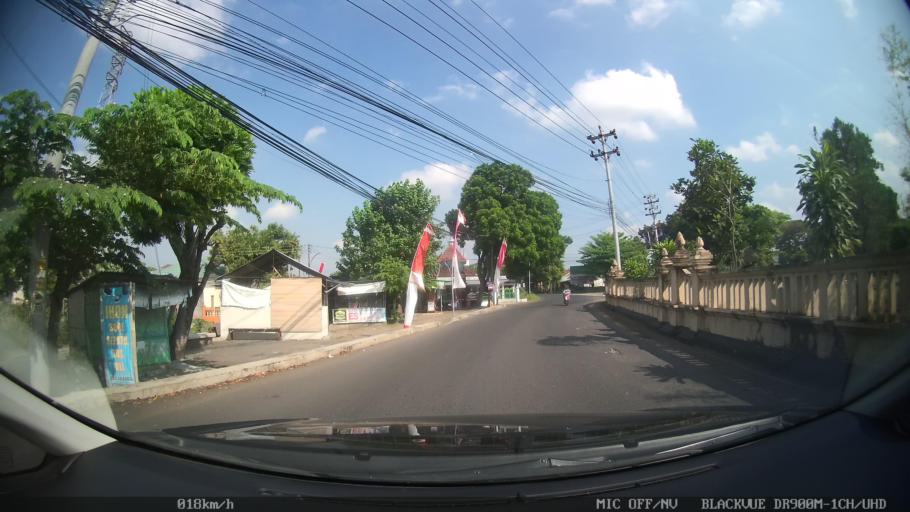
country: ID
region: Daerah Istimewa Yogyakarta
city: Melati
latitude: -7.7551
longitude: 110.3880
